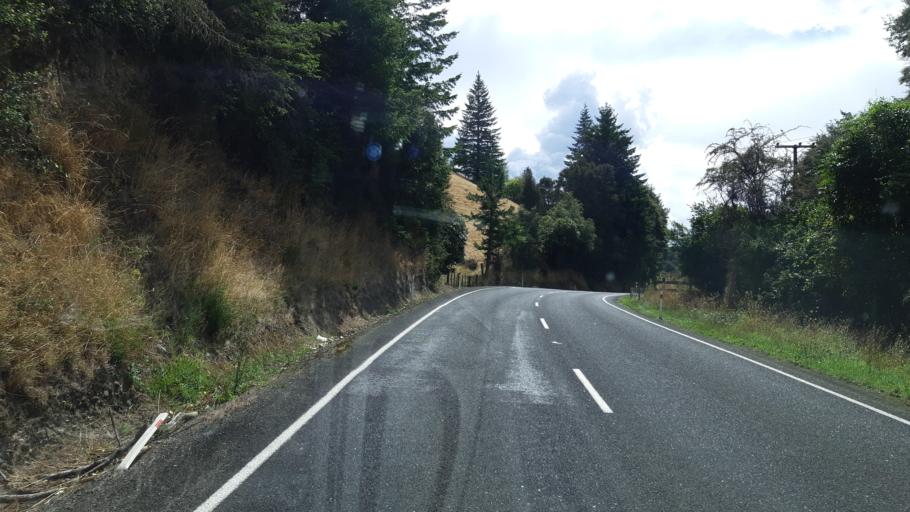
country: NZ
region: Tasman
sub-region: Tasman District
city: Wakefield
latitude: -41.5010
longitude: 172.7950
